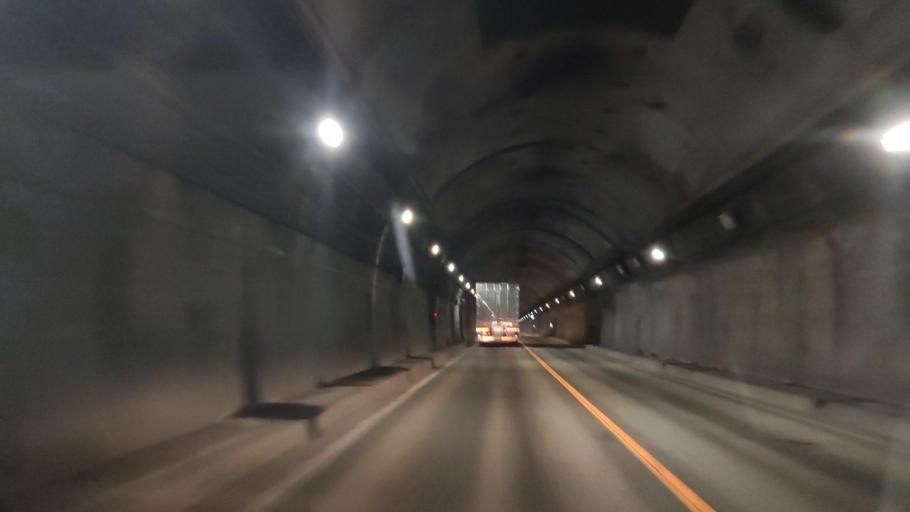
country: JP
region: Aomori
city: Aomori Shi
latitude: 40.7763
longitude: 140.9673
